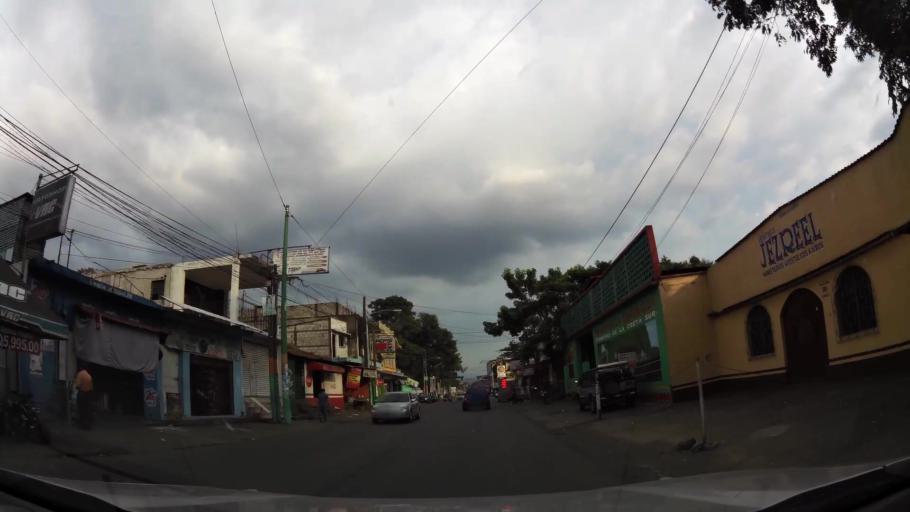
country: GT
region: Escuintla
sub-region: Municipio de Escuintla
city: Escuintla
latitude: 14.3077
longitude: -90.7851
